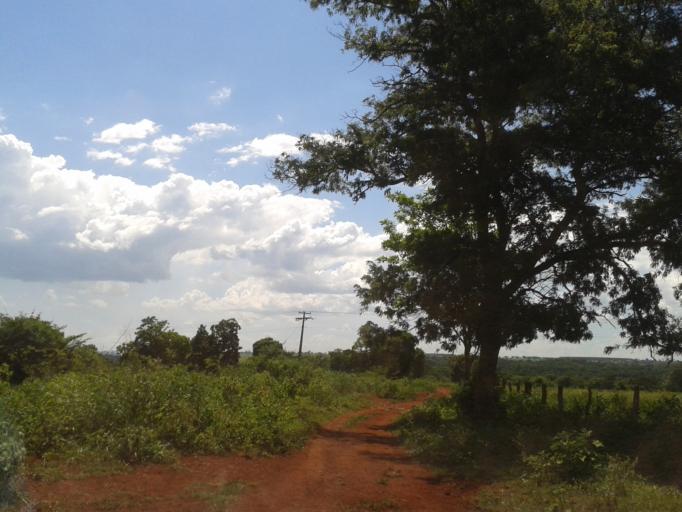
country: BR
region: Minas Gerais
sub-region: Santa Vitoria
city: Santa Vitoria
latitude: -19.1036
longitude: -50.5249
